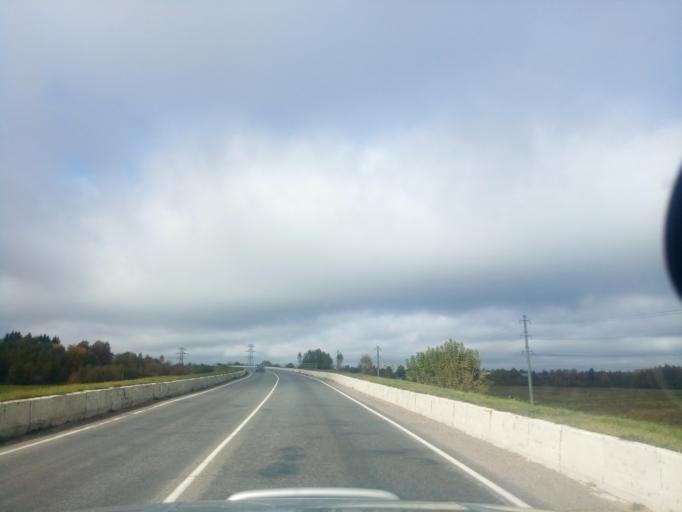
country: BY
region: Minsk
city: Zaslawye
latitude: 53.9974
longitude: 27.2884
